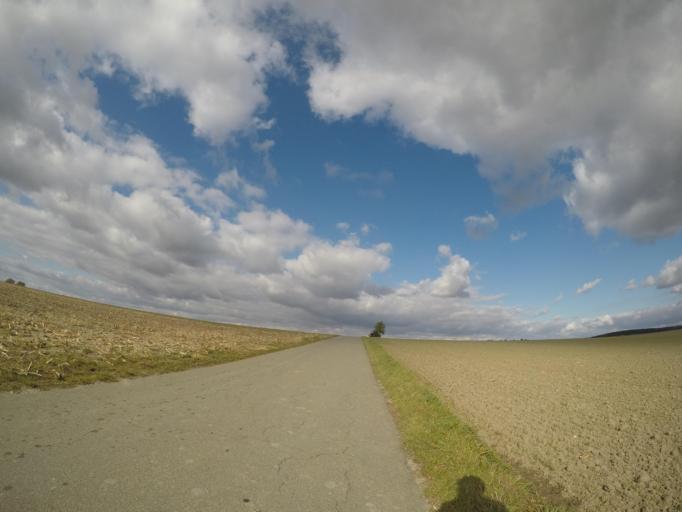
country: DE
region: Baden-Wuerttemberg
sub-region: Tuebingen Region
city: Unterstadion
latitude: 48.1954
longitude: 9.7012
